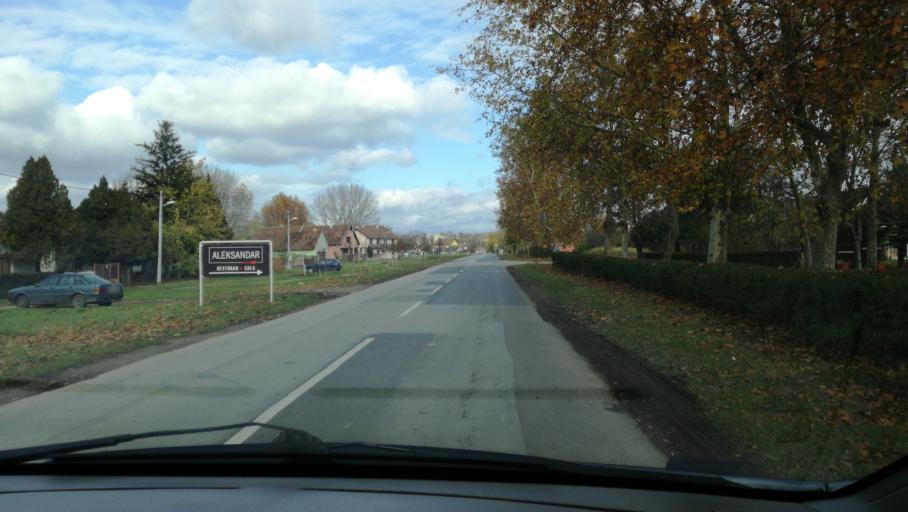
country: RS
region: Autonomna Pokrajina Vojvodina
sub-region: Severnobanatski Okrug
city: Kikinda
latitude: 45.8120
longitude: 20.4483
